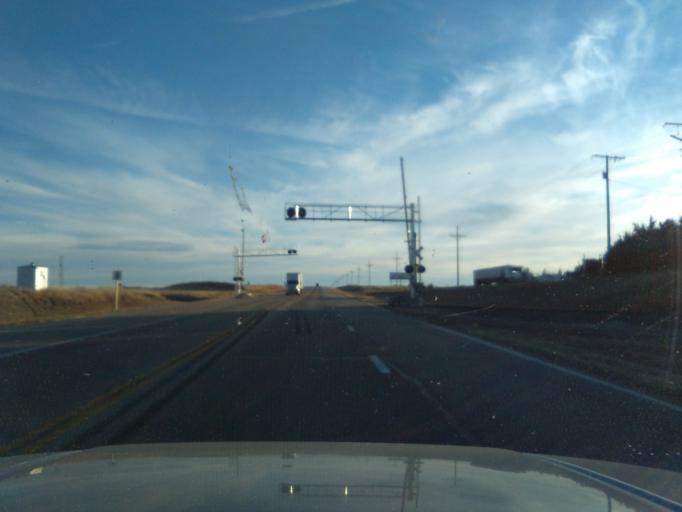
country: US
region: Kansas
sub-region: Logan County
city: Oakley
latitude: 39.1443
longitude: -100.8681
